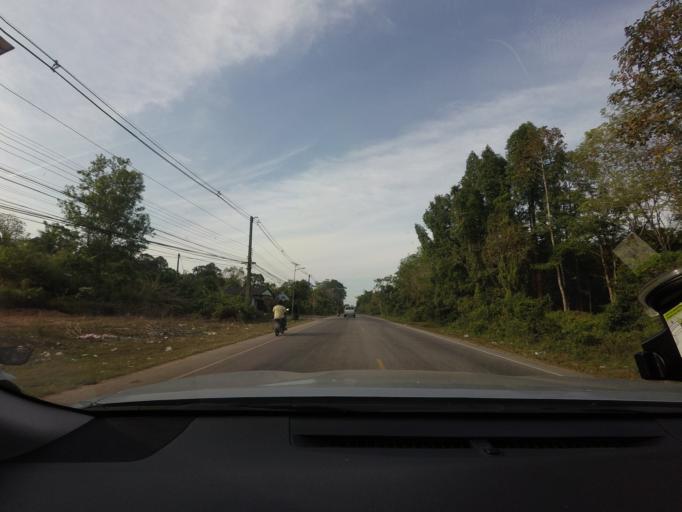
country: TH
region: Narathiwat
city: Ra-ngae
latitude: 6.3053
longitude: 101.7277
